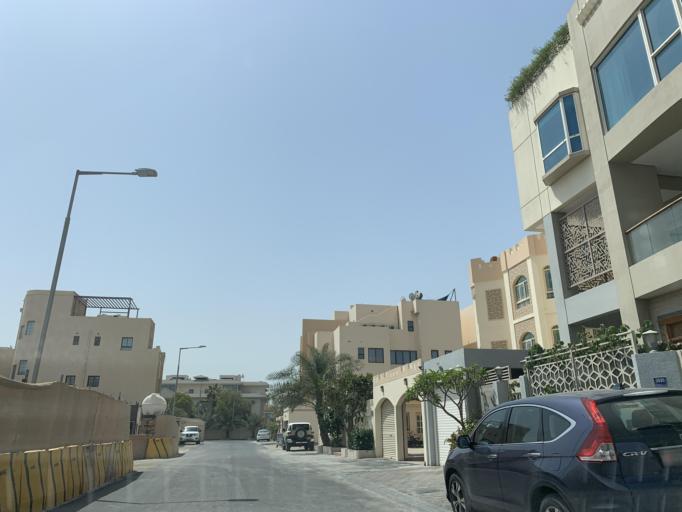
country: BH
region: Manama
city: Manama
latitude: 26.2030
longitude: 50.5744
